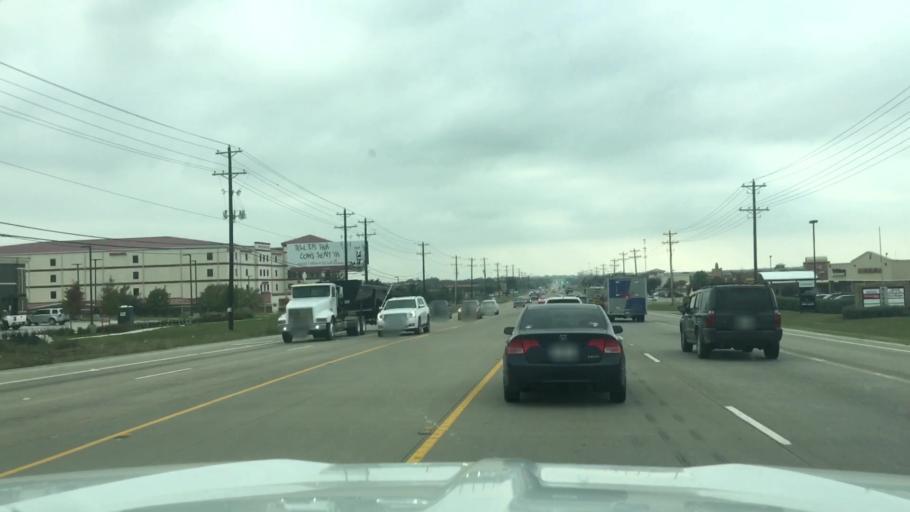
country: US
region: Texas
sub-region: Denton County
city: Little Elm
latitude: 33.2209
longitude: -96.9318
